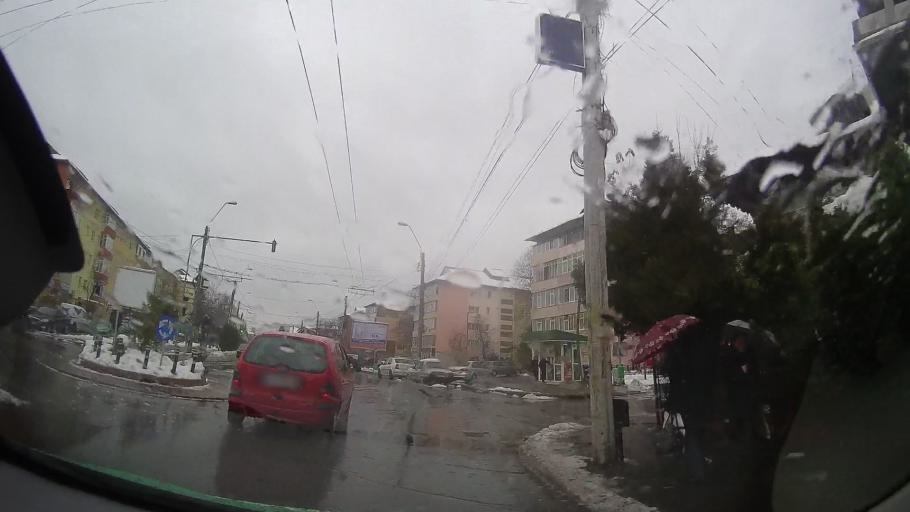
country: RO
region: Neamt
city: Piatra Neamt
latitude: 46.9341
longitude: 26.3584
